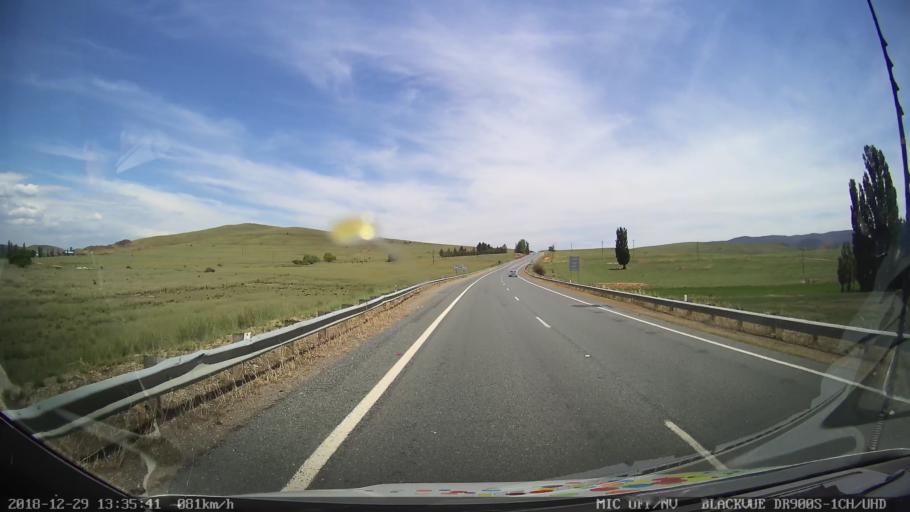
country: AU
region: New South Wales
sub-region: Cooma-Monaro
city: Cooma
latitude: -35.9624
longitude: 149.1480
